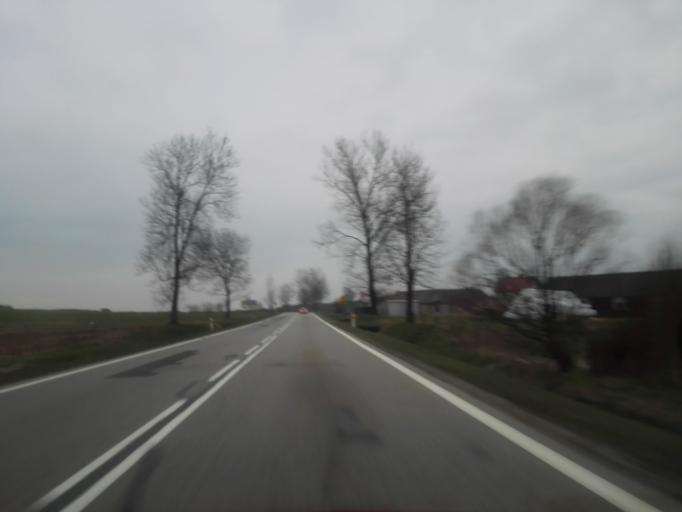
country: PL
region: Podlasie
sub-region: Powiat kolnenski
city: Stawiski
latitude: 53.2956
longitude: 22.1463
